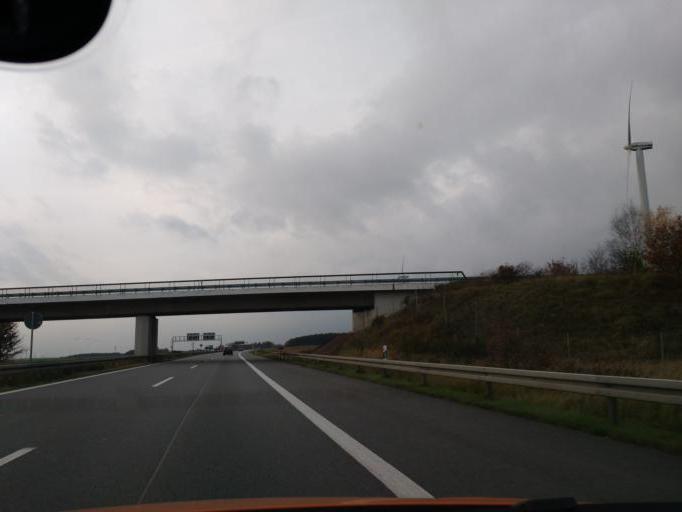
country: DE
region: Brandenburg
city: Wittstock
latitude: 53.1357
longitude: 12.4487
